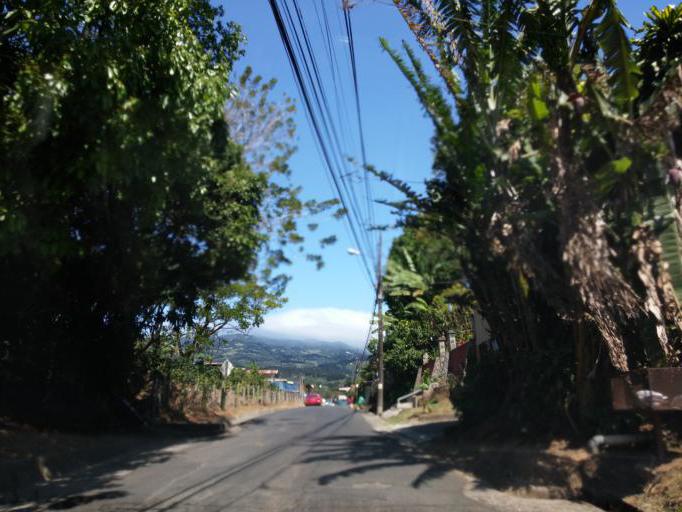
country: CR
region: Heredia
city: Santo Domingo
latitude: 10.0490
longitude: -84.1406
